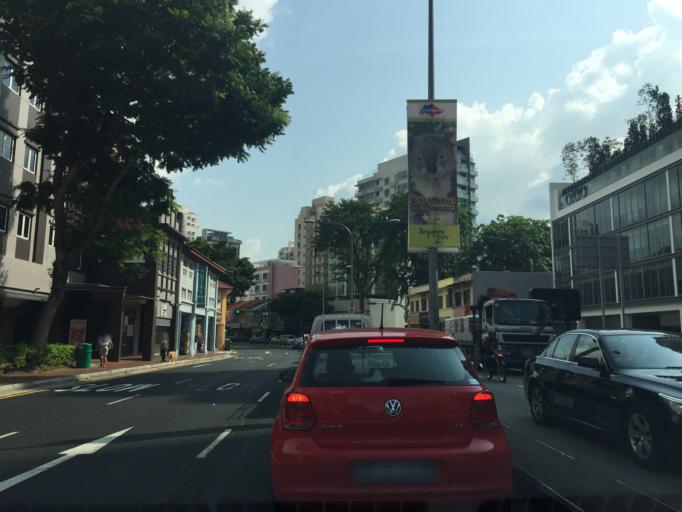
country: SG
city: Singapore
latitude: 1.3217
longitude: 103.8529
